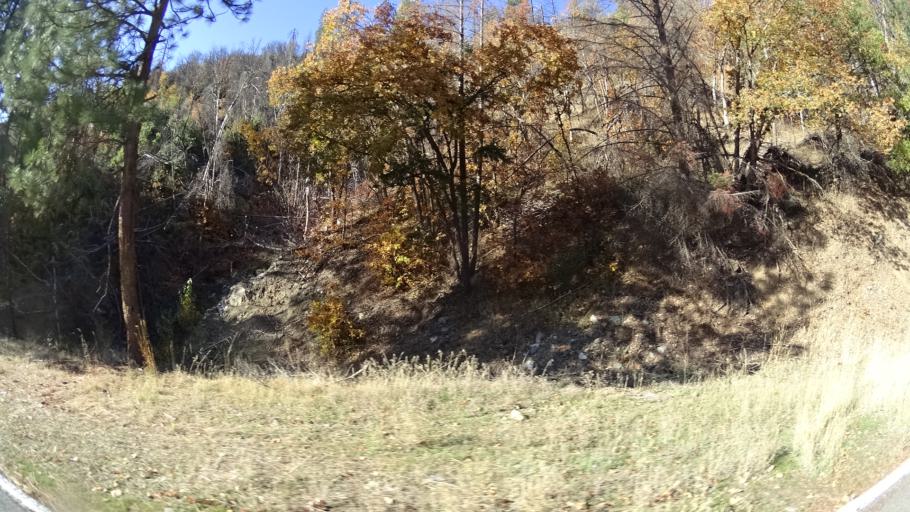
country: US
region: California
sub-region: Siskiyou County
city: Yreka
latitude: 41.8846
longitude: -122.8234
